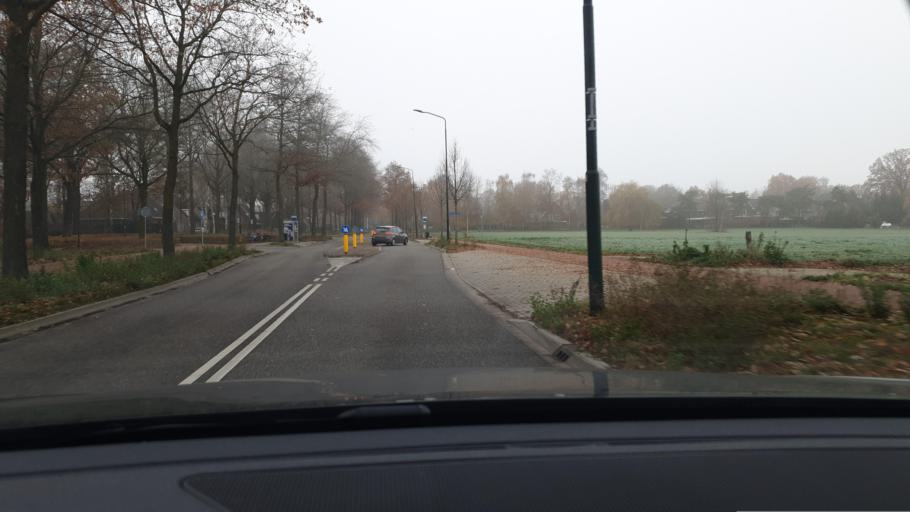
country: NL
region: North Brabant
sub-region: Gemeente Bladel en Netersel
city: Bladel
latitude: 51.3759
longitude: 5.2270
